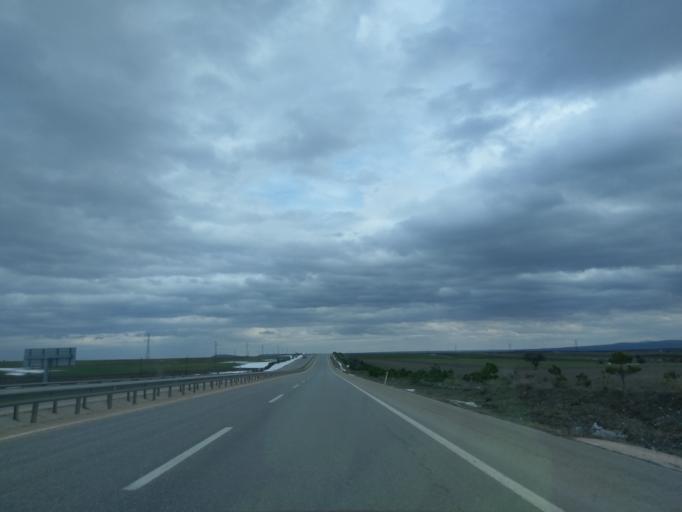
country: TR
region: Eskisehir
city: Inonu
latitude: 39.7260
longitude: 30.3058
